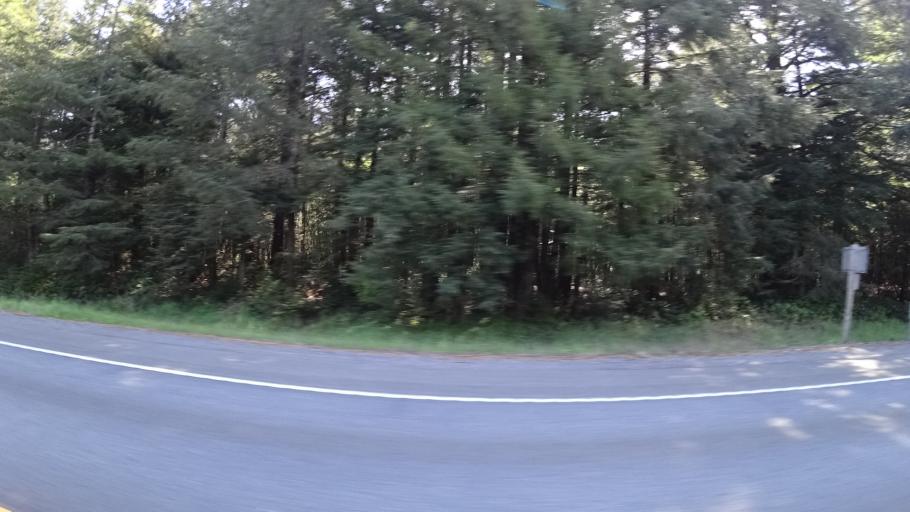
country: US
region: California
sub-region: Del Norte County
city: Bertsch-Oceanview
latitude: 41.8126
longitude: -124.1467
